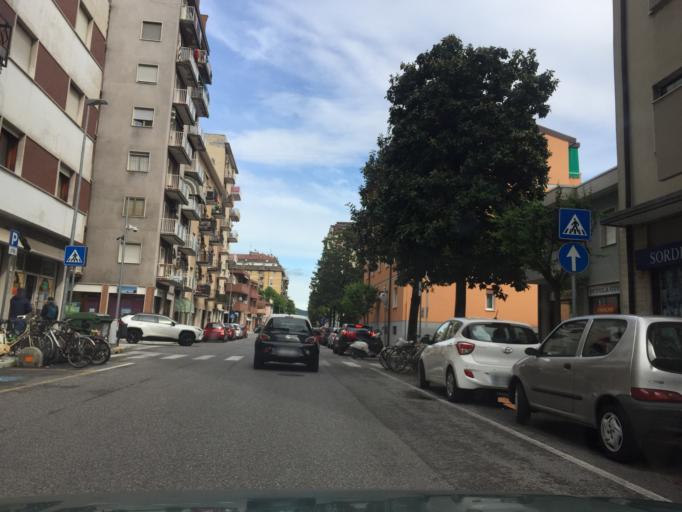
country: IT
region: Friuli Venezia Giulia
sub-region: Provincia di Gorizia
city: Monfalcone
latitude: 45.8069
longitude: 13.5317
